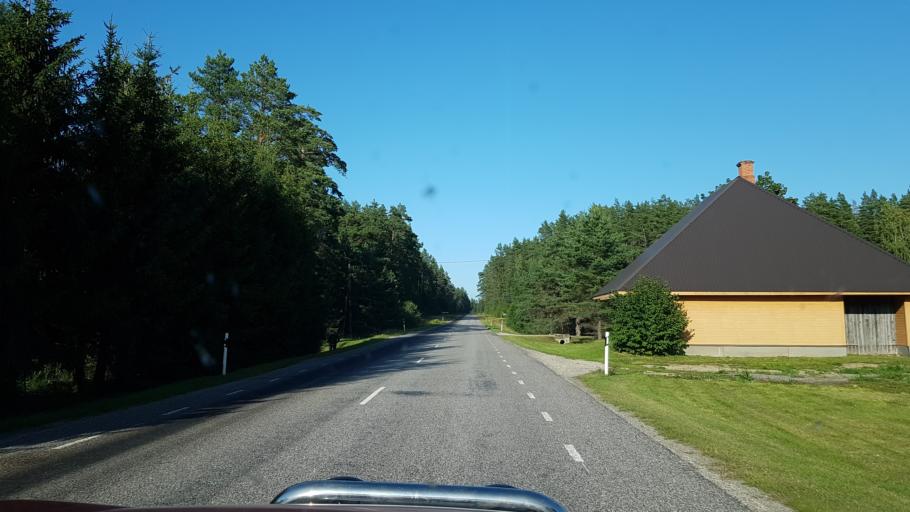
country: RU
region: Pskov
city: Pechory
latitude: 57.8172
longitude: 27.3385
